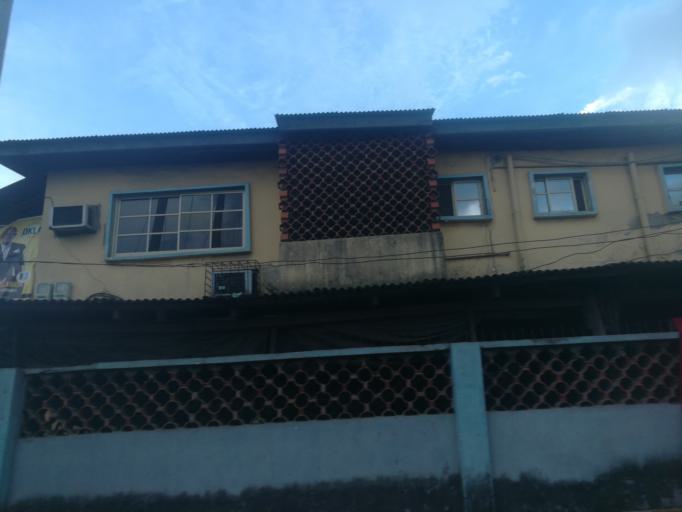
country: NG
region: Lagos
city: Ojota
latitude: 6.5639
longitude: 3.3697
